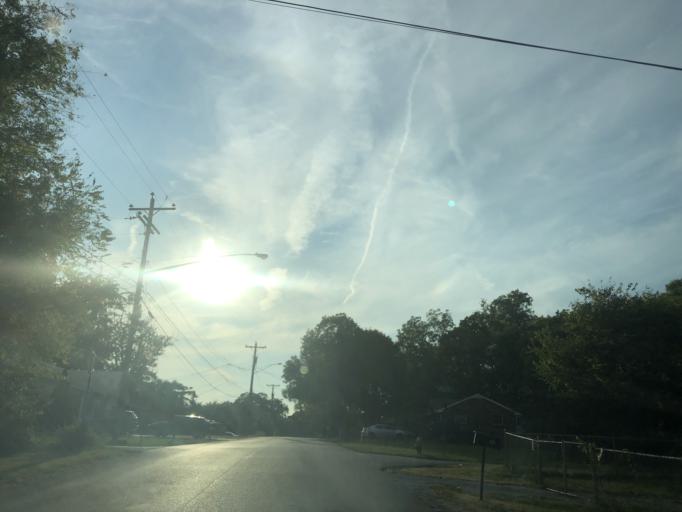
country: US
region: Tennessee
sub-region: Davidson County
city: Oak Hill
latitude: 36.1171
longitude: -86.7409
